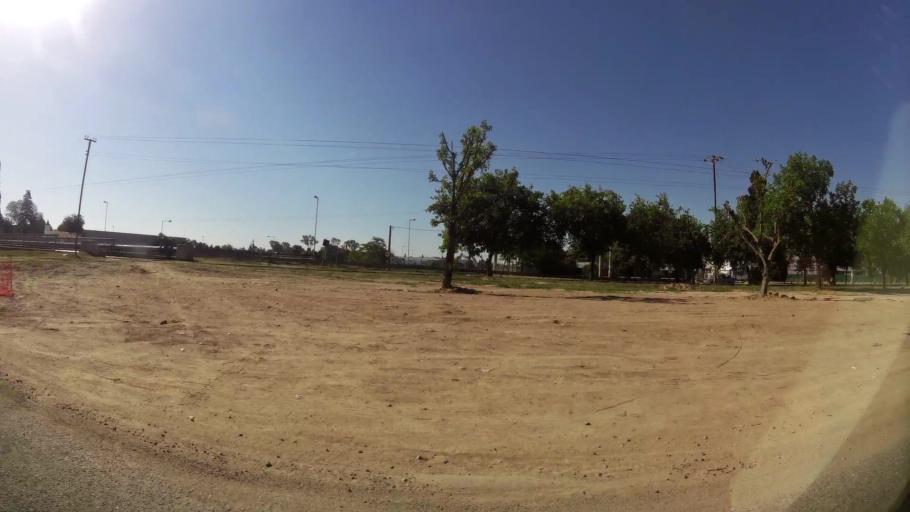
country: AR
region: Cordoba
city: Malvinas Argentinas
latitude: -31.3873
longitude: -64.1257
